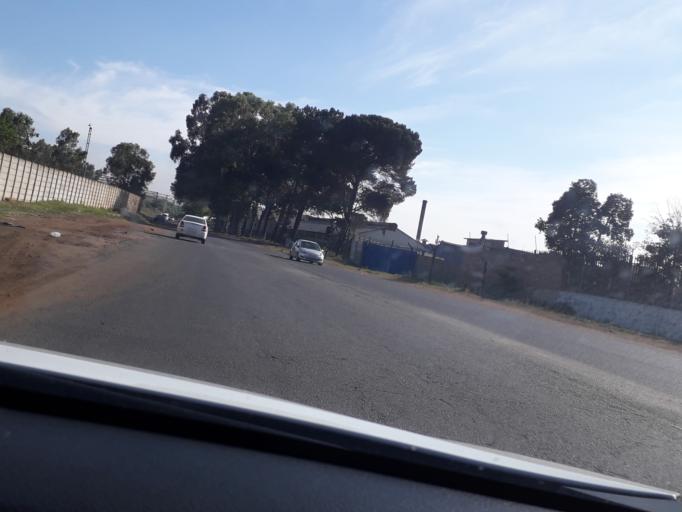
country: ZA
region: Gauteng
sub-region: Ekurhuleni Metropolitan Municipality
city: Boksburg
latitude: -26.1657
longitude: 28.2069
